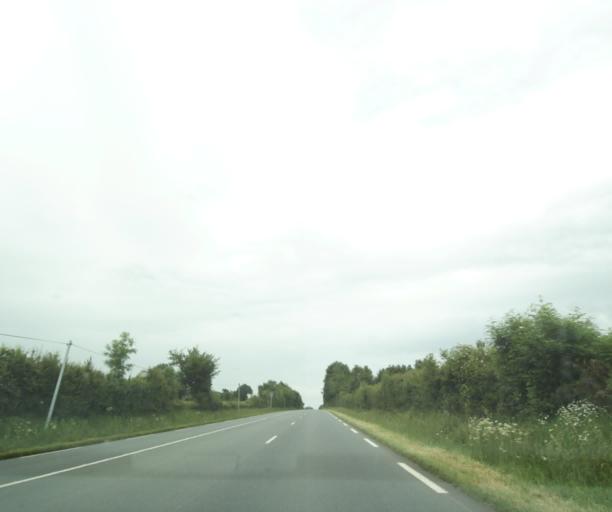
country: FR
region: Poitou-Charentes
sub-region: Departement des Deux-Sevres
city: Saint-Pardoux
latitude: 46.5922
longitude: -0.2908
